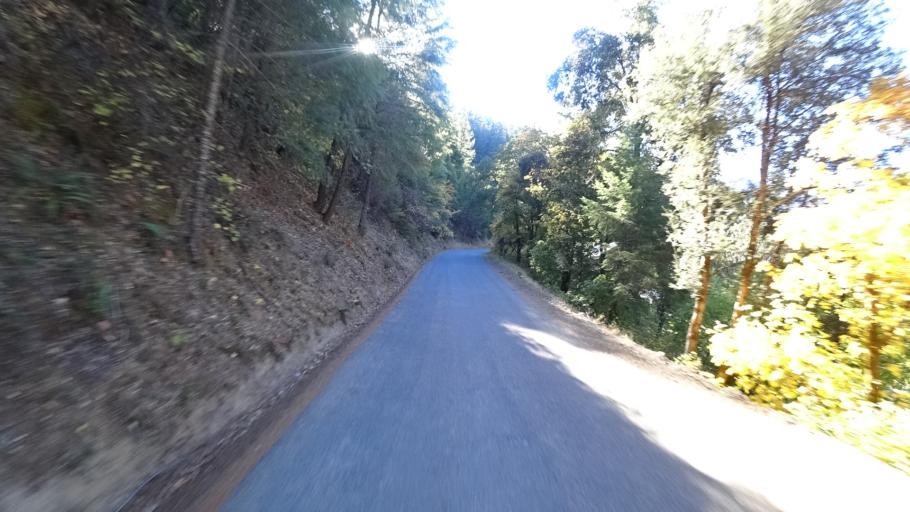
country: US
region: California
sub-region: Humboldt County
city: Willow Creek
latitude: 41.2519
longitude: -123.3119
